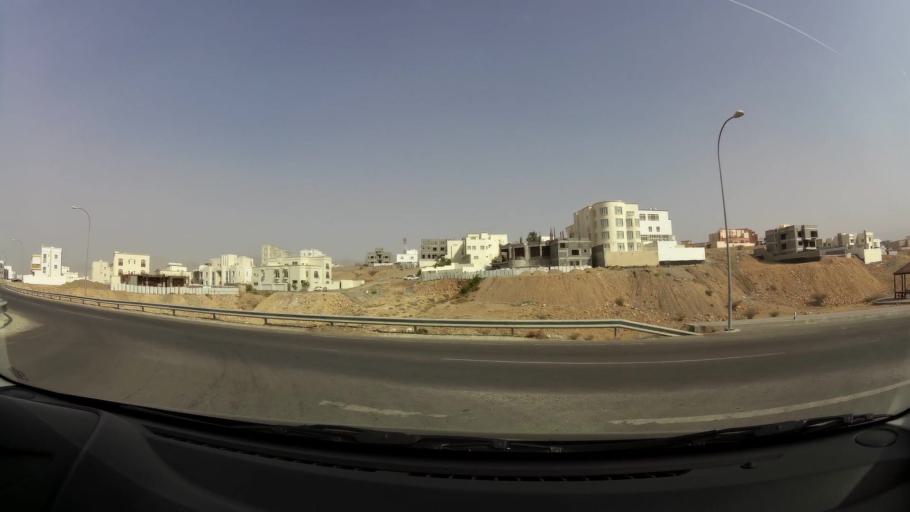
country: OM
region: Muhafazat Masqat
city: Bawshar
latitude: 23.5601
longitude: 58.3532
